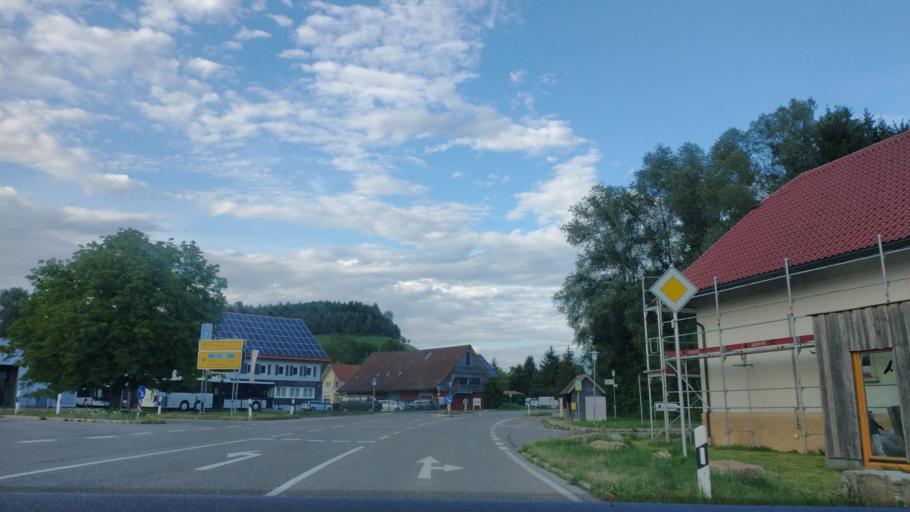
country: DE
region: Bavaria
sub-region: Swabia
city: Hergensweiler
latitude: 47.6533
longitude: 9.7773
